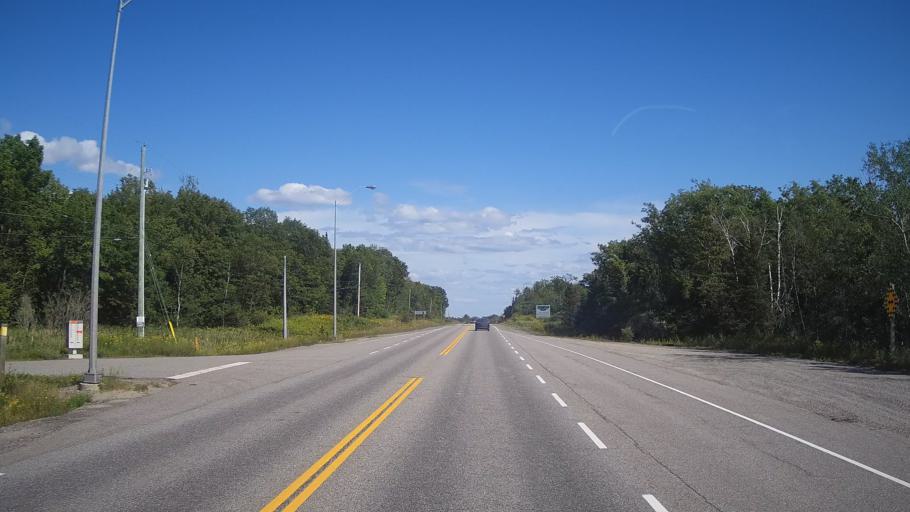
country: CA
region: Ontario
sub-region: Nipissing District
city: North Bay
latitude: 46.3562
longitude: -79.6480
